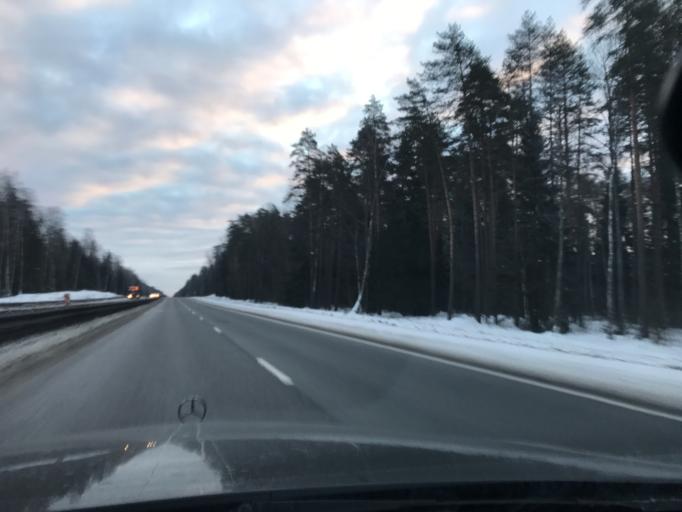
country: RU
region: Vladimir
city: Stepantsevo
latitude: 56.2221
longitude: 41.5453
